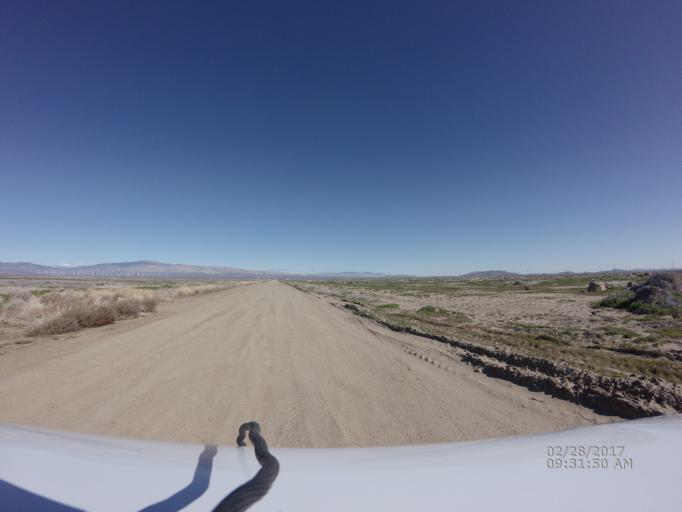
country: US
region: California
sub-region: Los Angeles County
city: Green Valley
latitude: 34.8051
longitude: -118.3613
